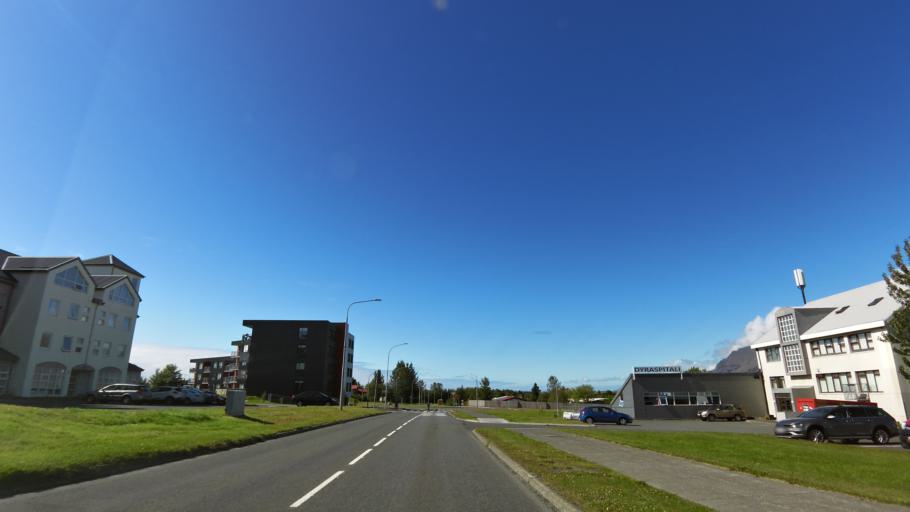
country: IS
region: Capital Region
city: Mosfellsbaer
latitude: 64.1680
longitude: -21.7004
